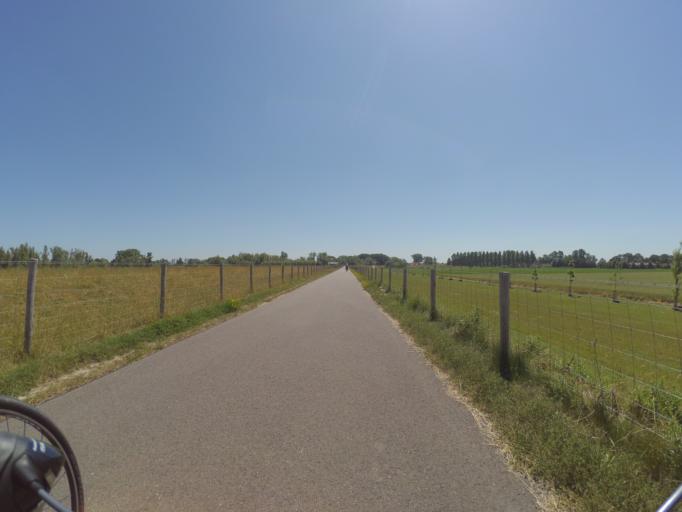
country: NL
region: South Holland
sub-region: Gemeente Sliedrecht
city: Sliedrecht
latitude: 51.7939
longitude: 4.7538
